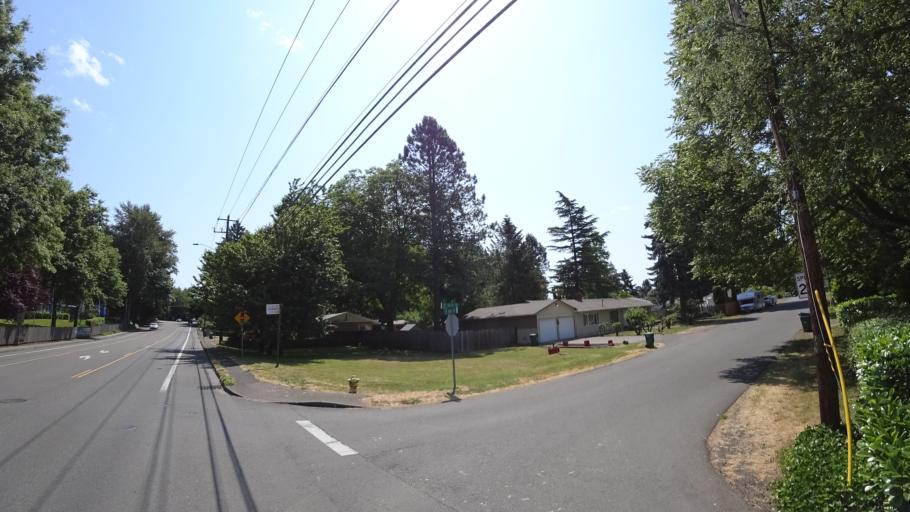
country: US
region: Oregon
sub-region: Clackamas County
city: Oatfield
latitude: 45.4479
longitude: -122.5954
